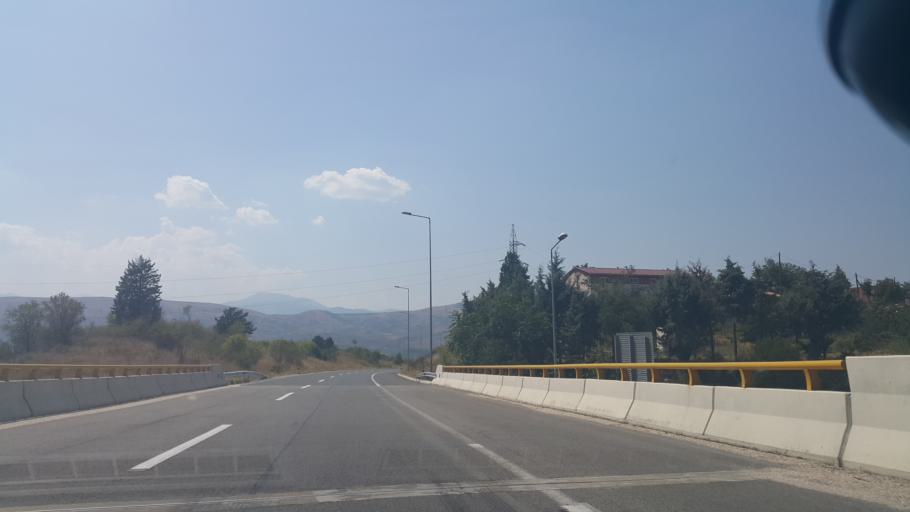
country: MK
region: Veles
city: Veles
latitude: 41.7287
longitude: 21.7944
